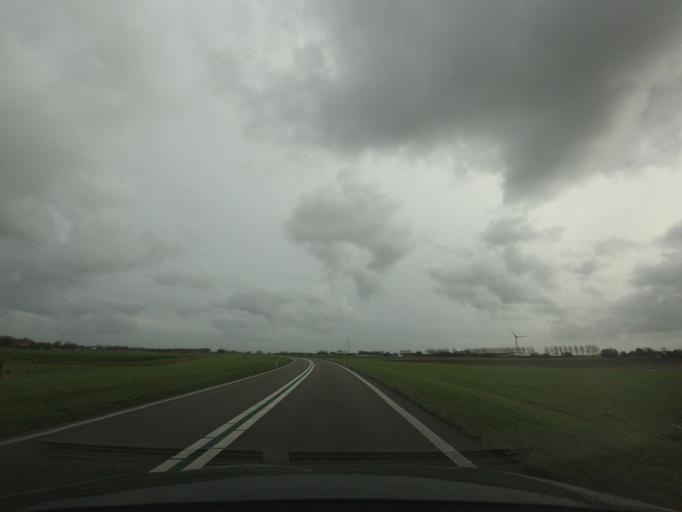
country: NL
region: North Holland
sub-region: Gemeente Heerhugowaard
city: Heerhugowaard
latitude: 52.7233
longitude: 4.8731
